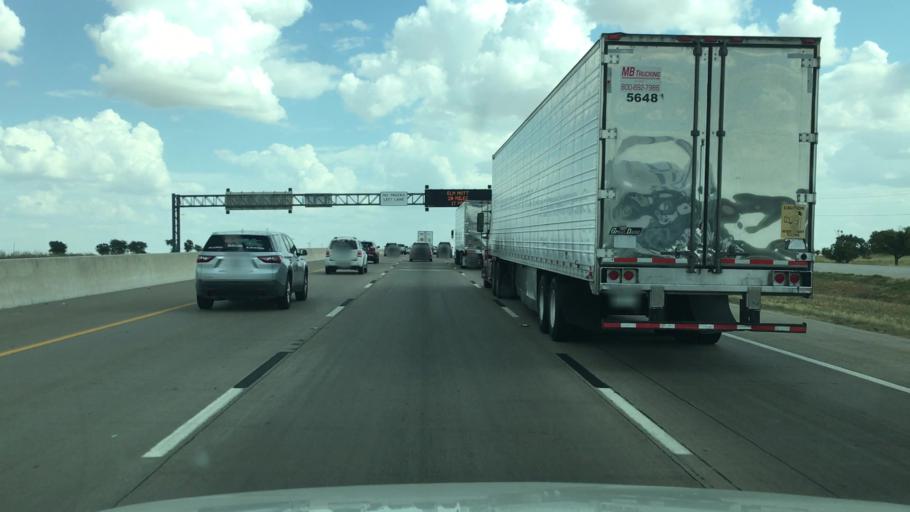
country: US
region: Texas
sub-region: Hill County
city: Hillsboro
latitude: 31.9497
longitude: -97.1122
